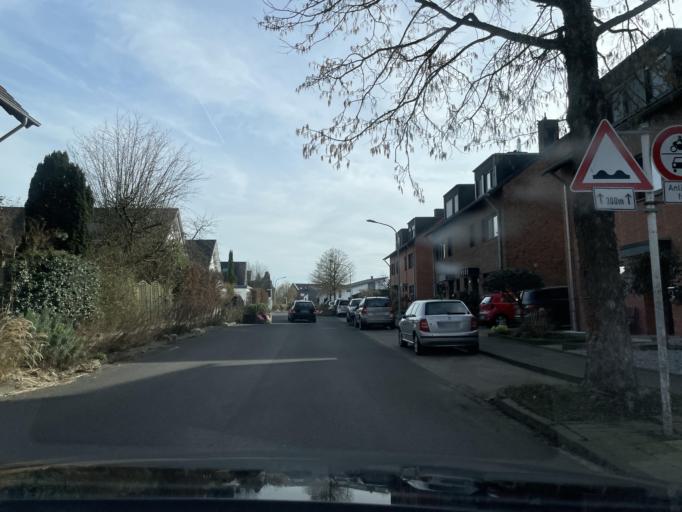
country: DE
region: North Rhine-Westphalia
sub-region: Regierungsbezirk Dusseldorf
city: Monchengladbach
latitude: 51.2284
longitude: 6.4512
